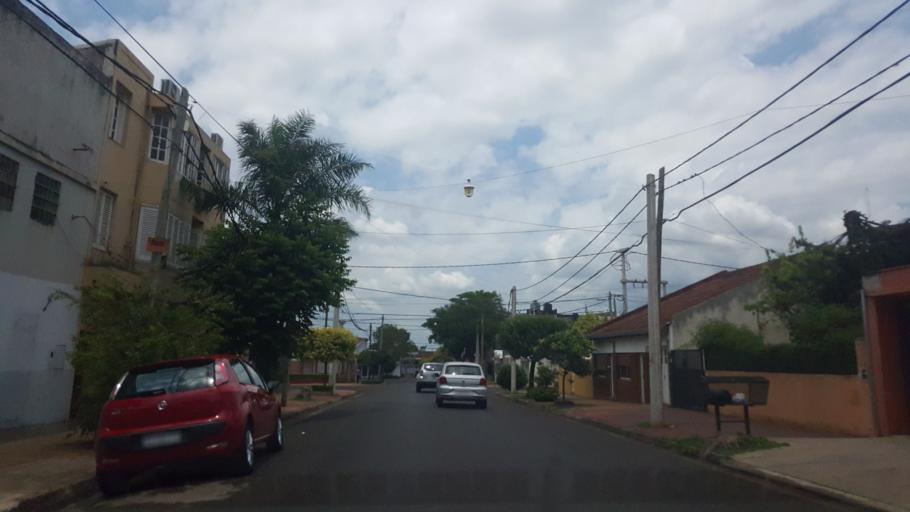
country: AR
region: Misiones
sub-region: Departamento de Capital
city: Posadas
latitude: -27.3768
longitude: -55.8970
